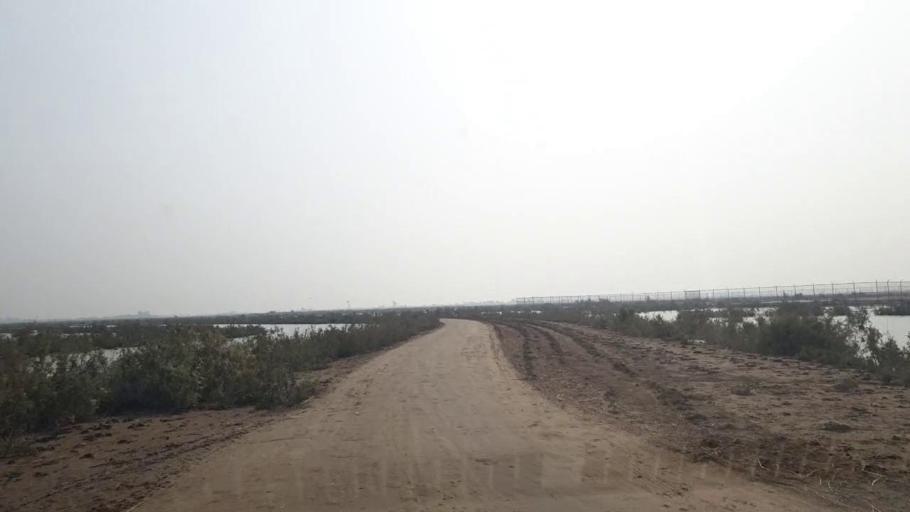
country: PK
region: Sindh
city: Matli
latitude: 25.1004
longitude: 68.6766
